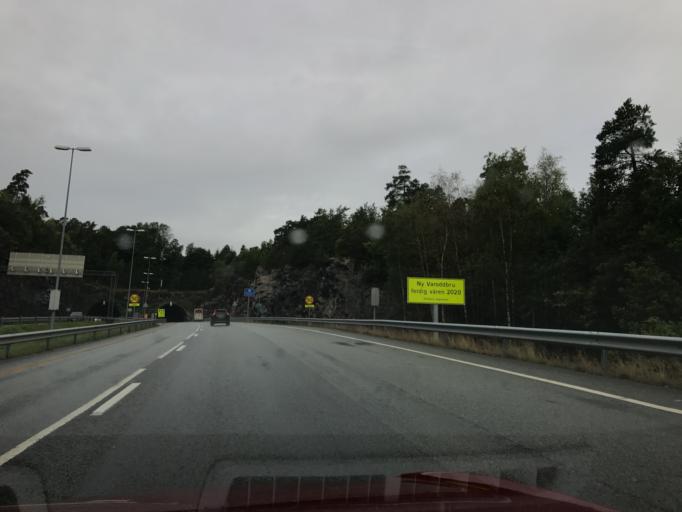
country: NO
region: Vest-Agder
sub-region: Kristiansand
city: Justvik
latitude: 58.1615
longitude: 8.0722
